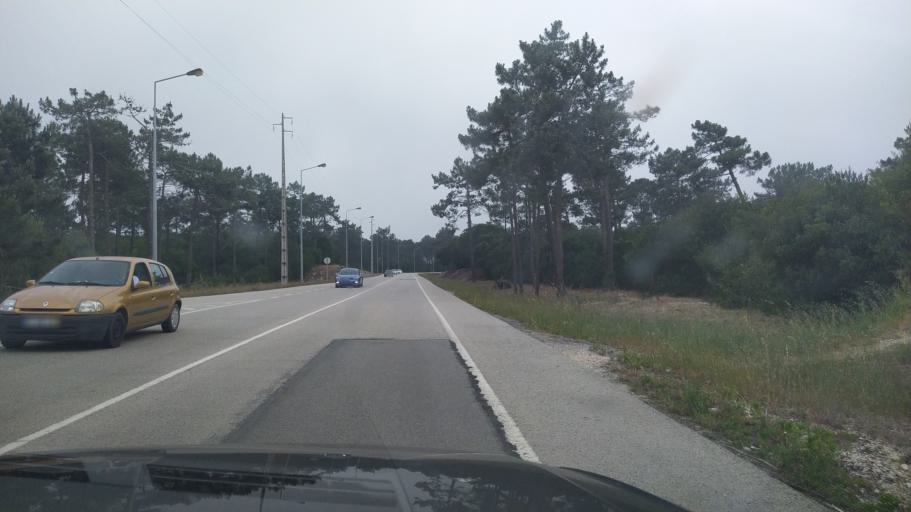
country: PT
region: Aveiro
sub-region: Ilhavo
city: Gafanha da Nazare
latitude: 40.6185
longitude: -8.7146
